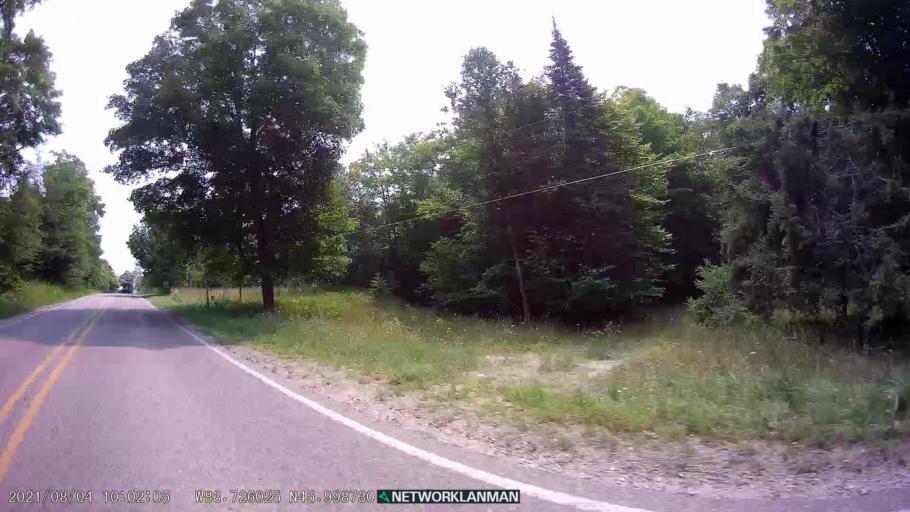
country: CA
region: Ontario
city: Thessalon
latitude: 45.9987
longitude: -83.7258
